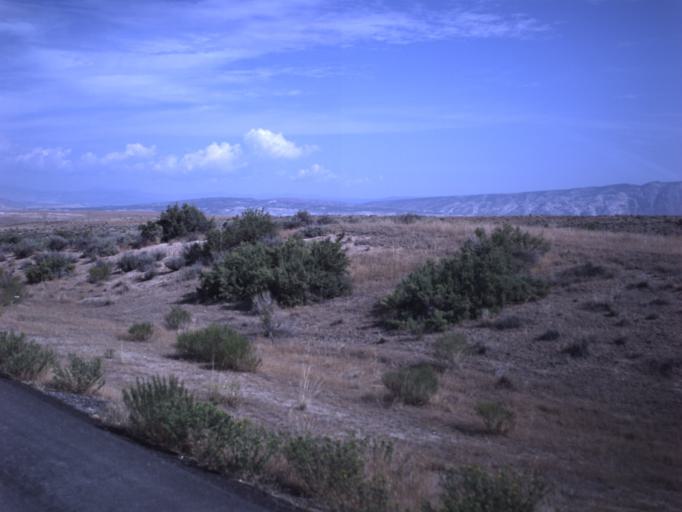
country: US
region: Utah
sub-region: Uintah County
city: Naples
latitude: 40.3422
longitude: -109.2982
